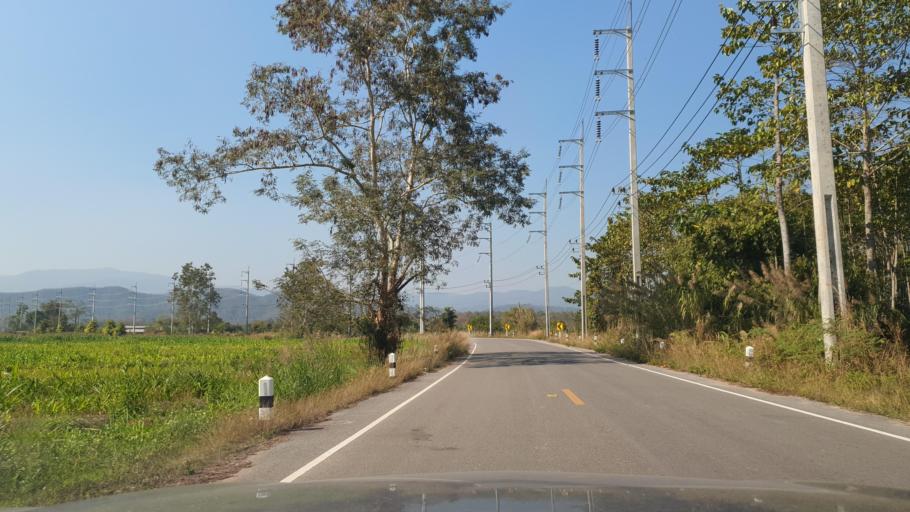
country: TH
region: Chiang Rai
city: Mae Lao
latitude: 19.8011
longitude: 99.6960
